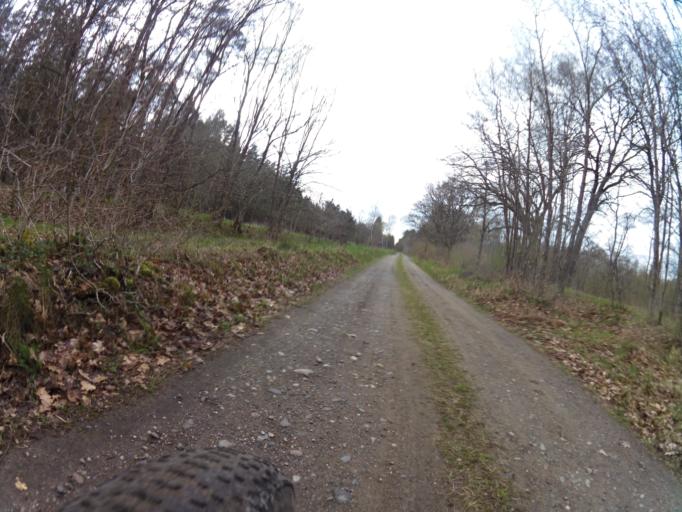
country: PL
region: West Pomeranian Voivodeship
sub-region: Powiat slawienski
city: Slawno
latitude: 54.3221
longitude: 16.7665
